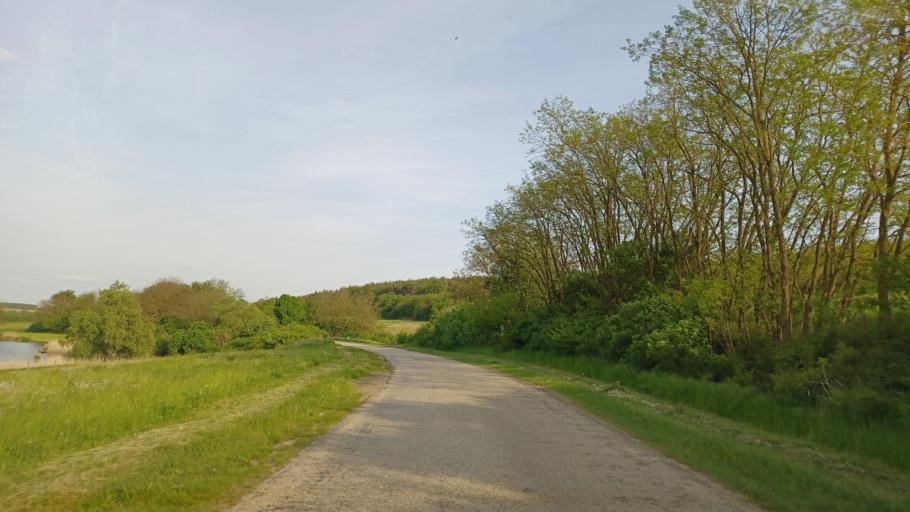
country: HU
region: Baranya
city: Kozarmisleny
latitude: 45.9646
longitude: 18.3682
